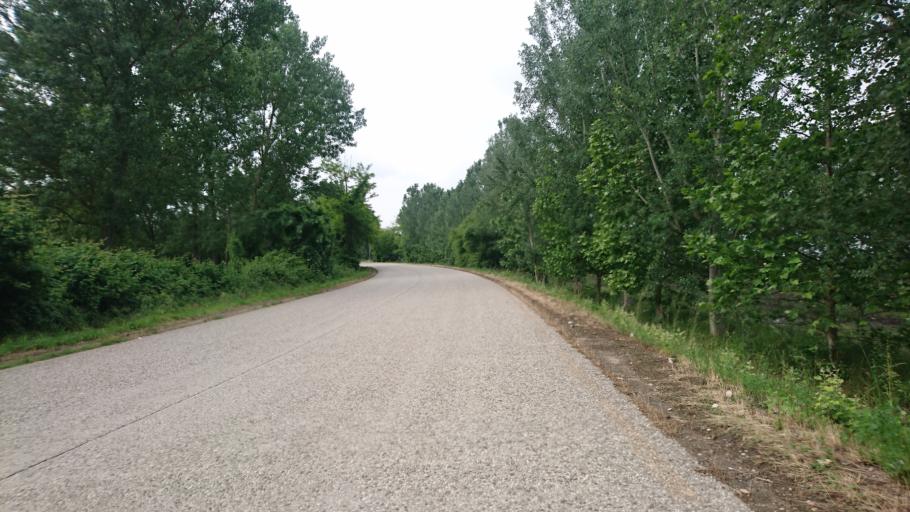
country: IT
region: Veneto
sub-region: Provincia di Padova
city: Monselice
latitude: 45.2312
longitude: 11.7205
